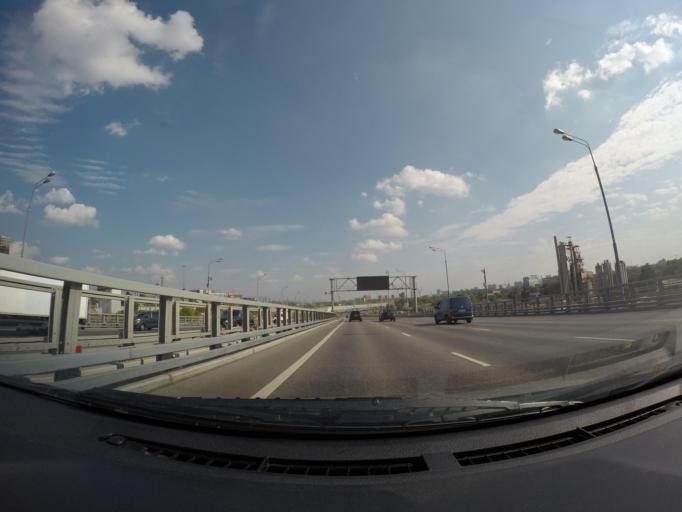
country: RU
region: Moscow
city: Zapadnoye Degunino
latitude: 55.8563
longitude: 37.5372
